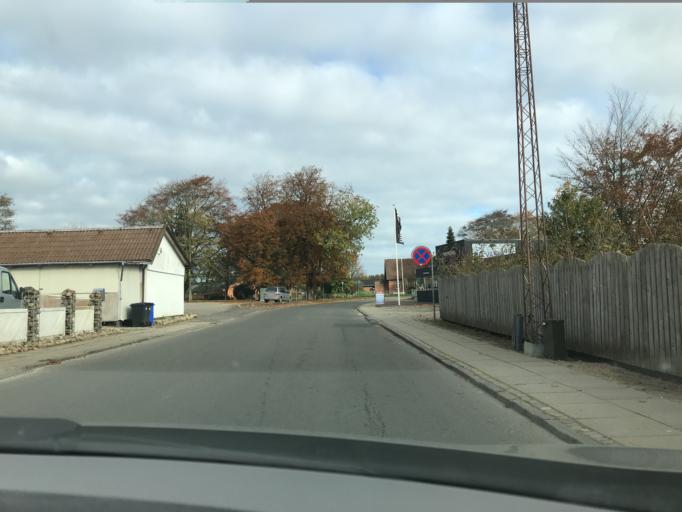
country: DK
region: South Denmark
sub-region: Vejle Kommune
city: Egtved
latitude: 55.6169
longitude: 9.3120
